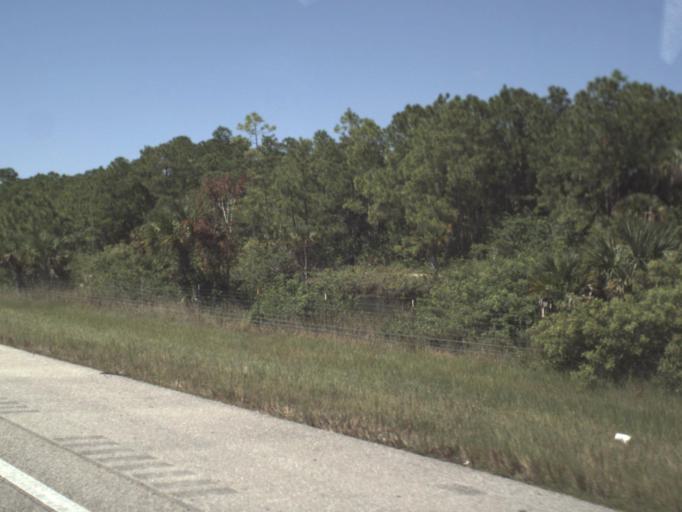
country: US
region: Florida
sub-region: Collier County
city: Orangetree
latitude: 26.1532
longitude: -81.5387
